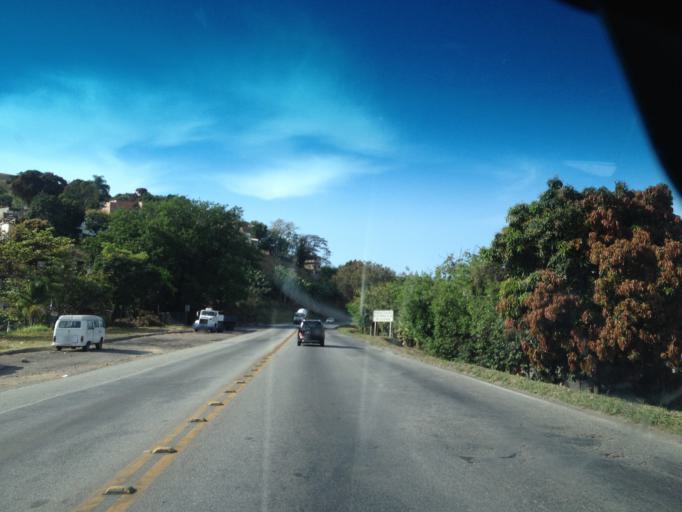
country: BR
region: Rio de Janeiro
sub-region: Volta Redonda
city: Volta Redonda
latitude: -22.5426
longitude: -44.1134
